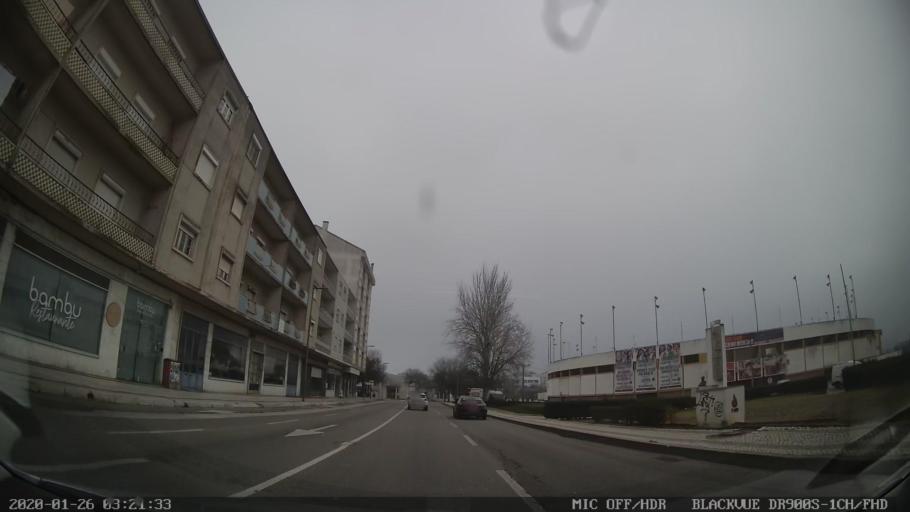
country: PT
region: Santarem
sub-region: Santarem
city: Santarem
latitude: 39.2296
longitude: -8.6876
